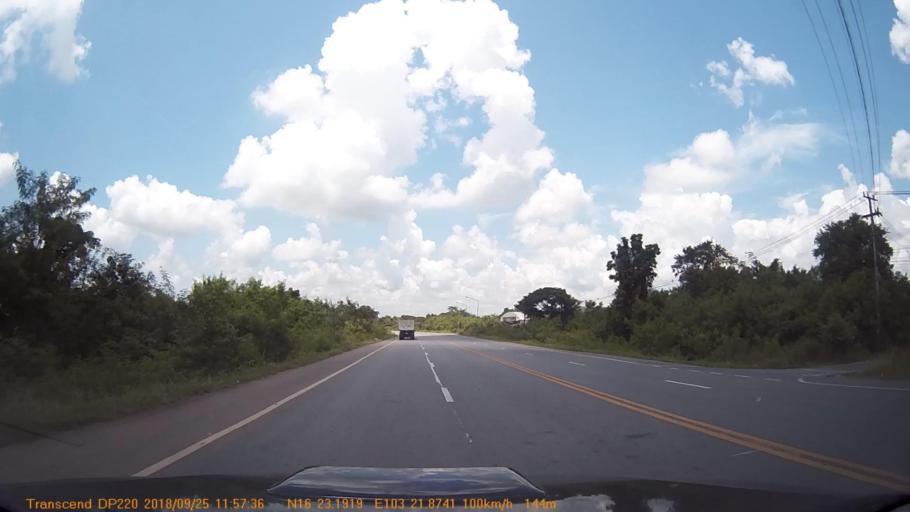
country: TH
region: Kalasin
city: Yang Talat
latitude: 16.3864
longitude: 103.3647
